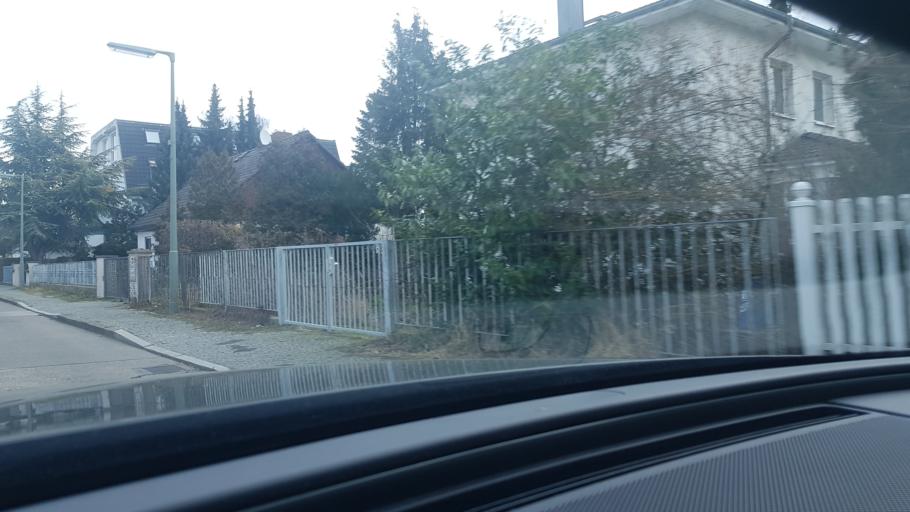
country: DE
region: Berlin
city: Mariendorf
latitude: 52.4204
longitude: 13.3859
